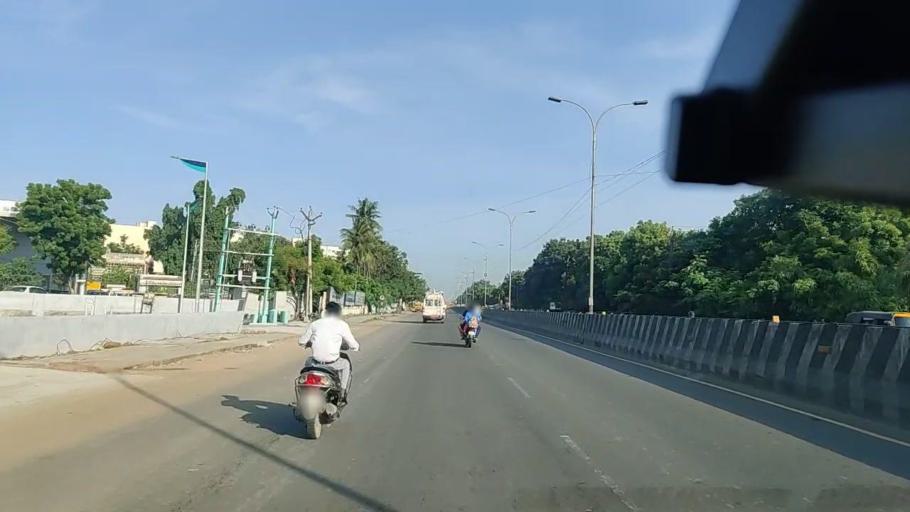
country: IN
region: Tamil Nadu
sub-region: Thiruvallur
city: Chinnasekkadu
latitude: 13.1371
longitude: 80.2302
